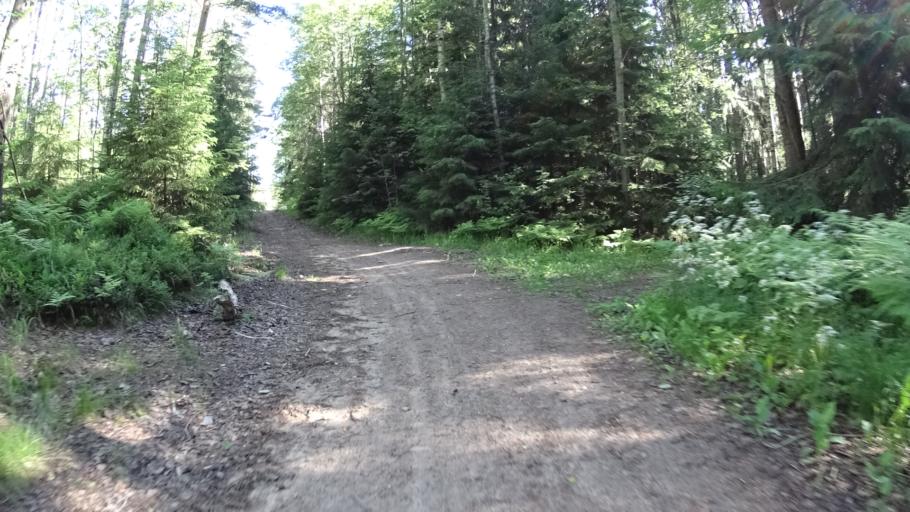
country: FI
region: Uusimaa
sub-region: Helsinki
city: Kilo
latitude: 60.2995
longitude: 24.8120
